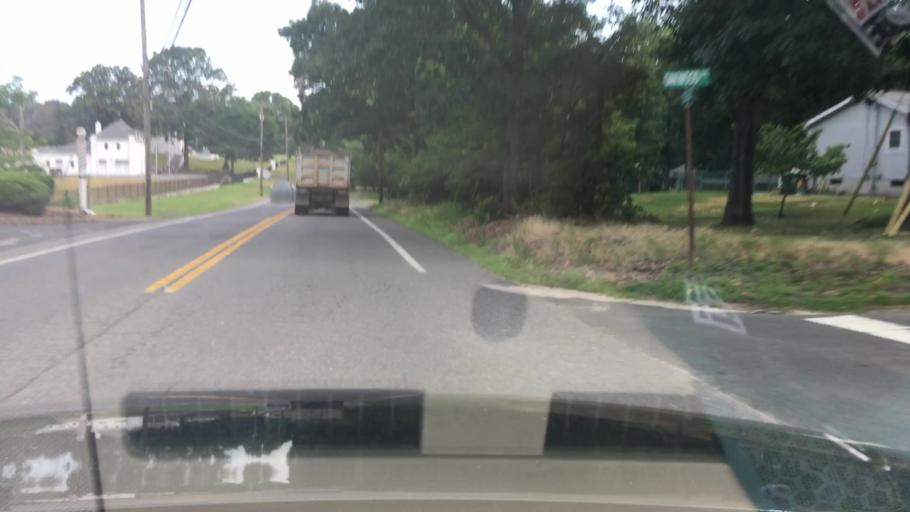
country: US
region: New Jersey
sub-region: Ocean County
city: Vista Center
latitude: 40.1220
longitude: -74.3936
